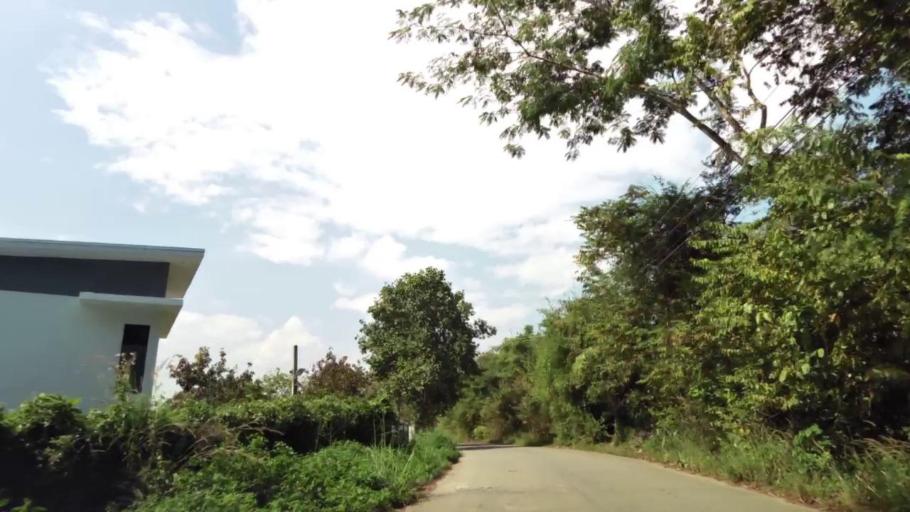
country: TH
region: Chiang Rai
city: Chiang Rai
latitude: 19.8867
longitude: 99.8102
